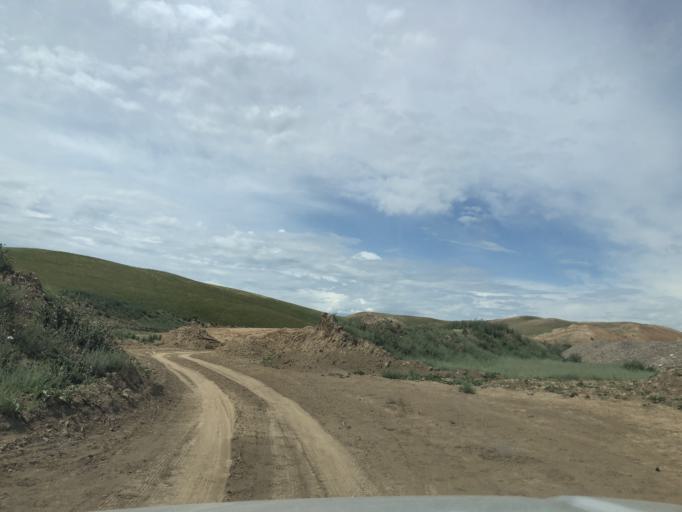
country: KZ
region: Almaty Oblysy
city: Burunday
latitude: 43.2963
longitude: 76.2000
